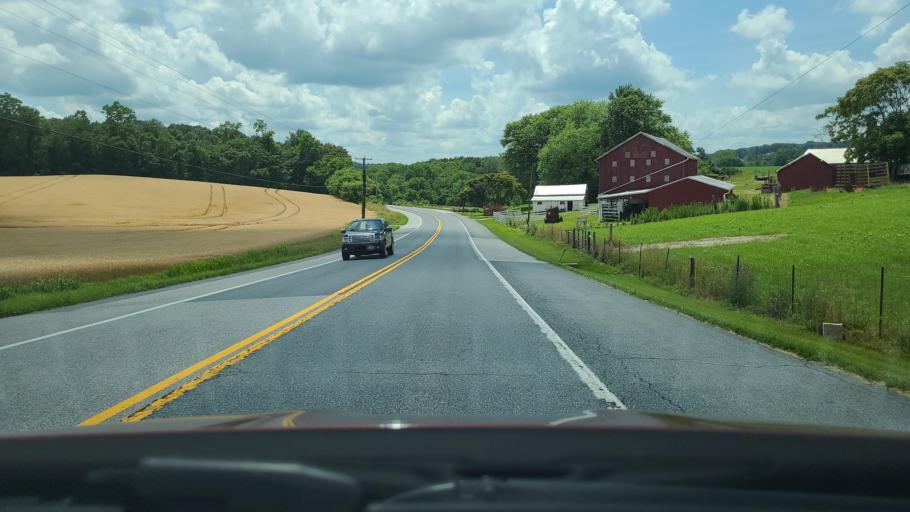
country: US
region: Maryland
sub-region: Carroll County
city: New Windsor
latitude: 39.5083
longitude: -77.0462
